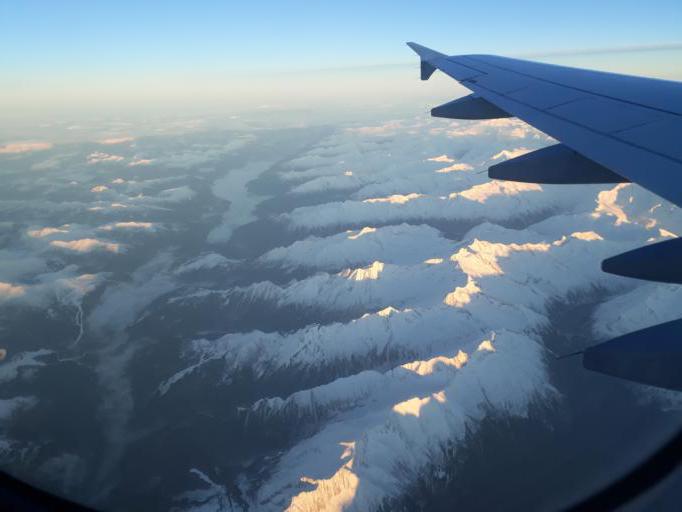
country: AT
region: Tyrol
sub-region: Politischer Bezirk Schwaz
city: Mayrhofen
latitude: 47.1570
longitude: 11.8851
